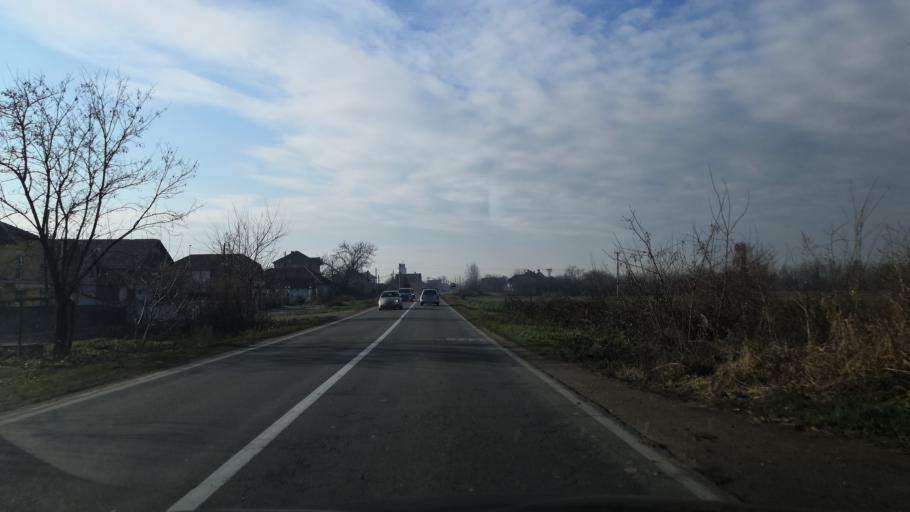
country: RS
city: Lesnica
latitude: 44.6598
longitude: 19.3239
